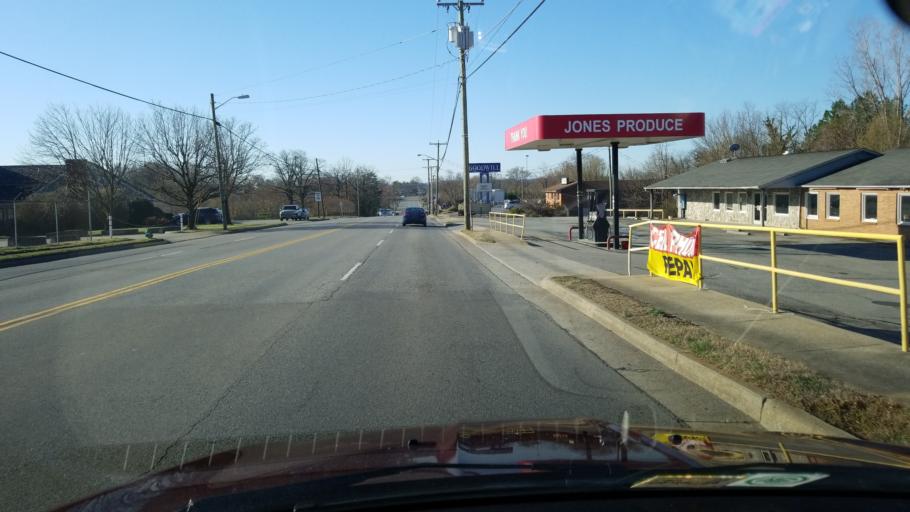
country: US
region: Virginia
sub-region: Franklin County
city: Rocky Mount
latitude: 37.0111
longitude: -79.8935
